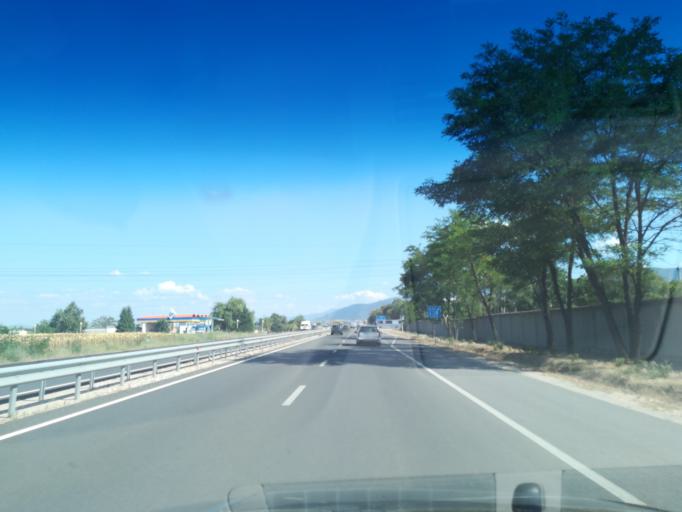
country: BG
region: Plovdiv
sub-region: Obshtina Asenovgrad
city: Asenovgrad
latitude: 42.0648
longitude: 24.8171
